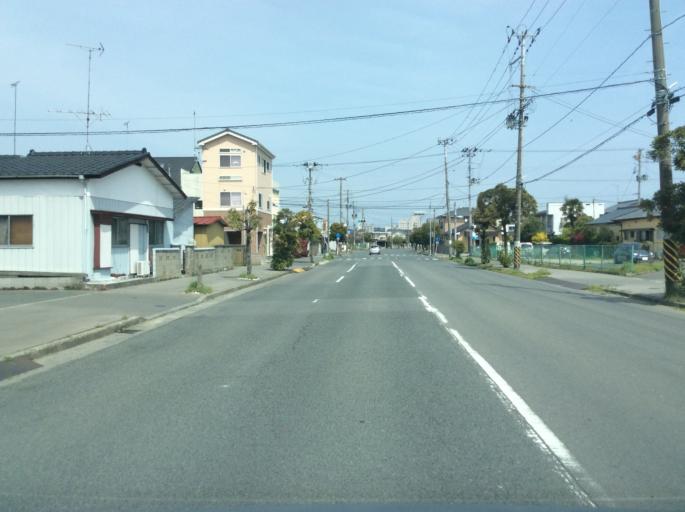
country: JP
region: Fukushima
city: Iwaki
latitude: 36.9490
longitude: 140.8924
